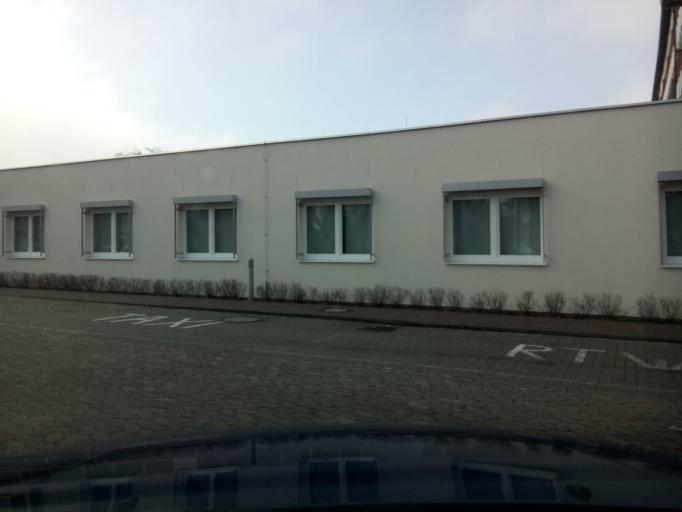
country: DE
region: Lower Saxony
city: Lilienthal
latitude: 53.1494
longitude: 8.9078
